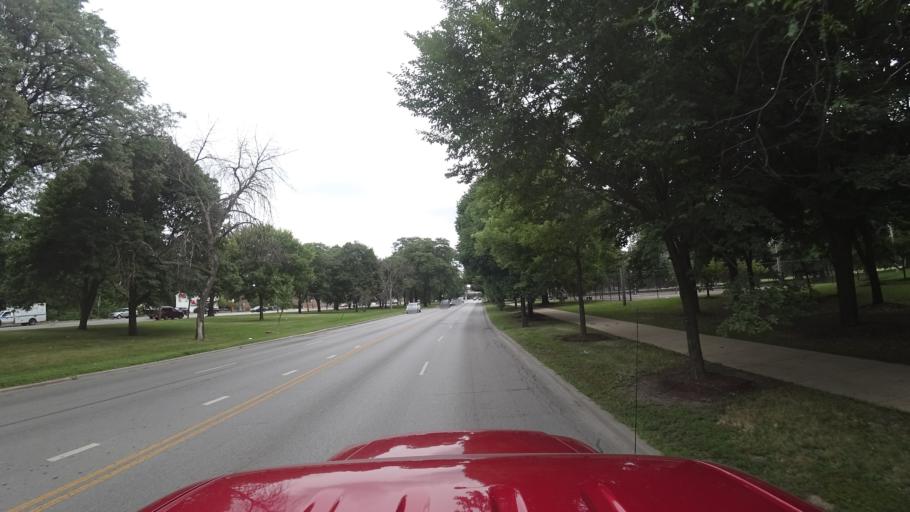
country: US
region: Illinois
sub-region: Cook County
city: Chicago
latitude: 41.8236
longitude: -87.6843
